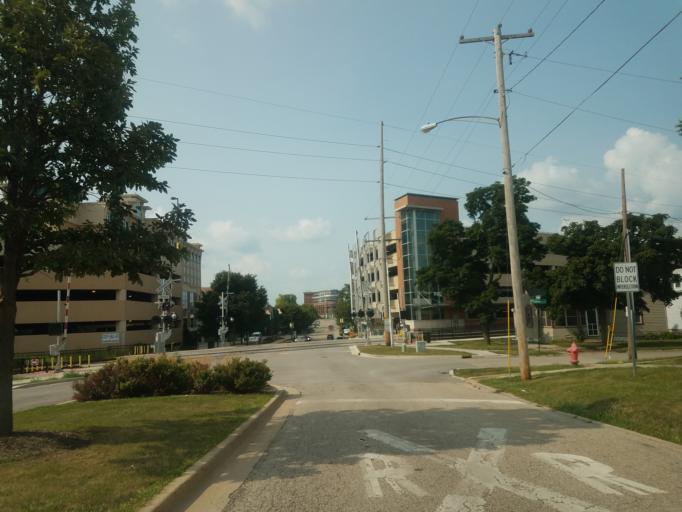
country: US
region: Illinois
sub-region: McLean County
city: Normal
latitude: 40.5073
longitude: -88.9857
